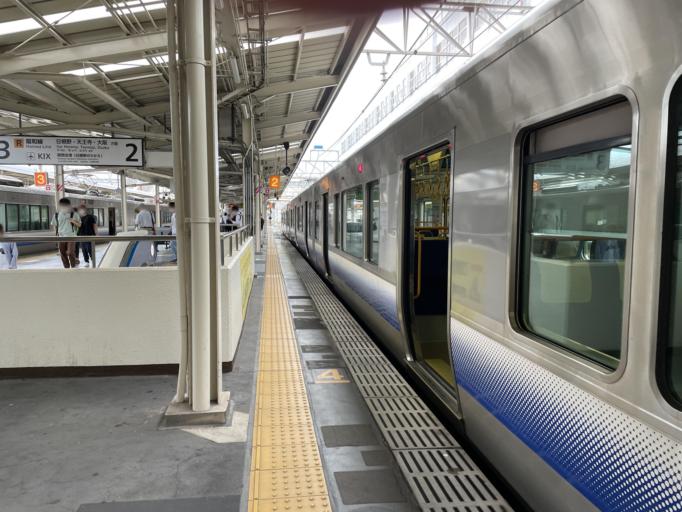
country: JP
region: Wakayama
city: Wakayama-shi
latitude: 34.2325
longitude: 135.1912
